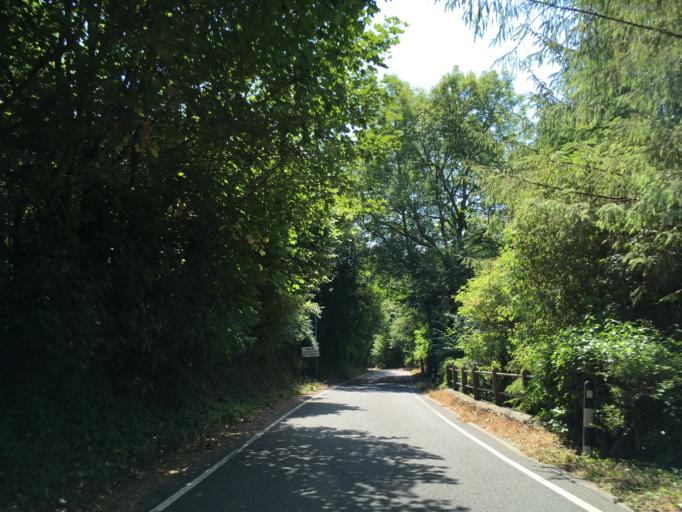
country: GB
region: England
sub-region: Gloucestershire
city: Brimscombe
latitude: 51.7329
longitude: -2.1744
